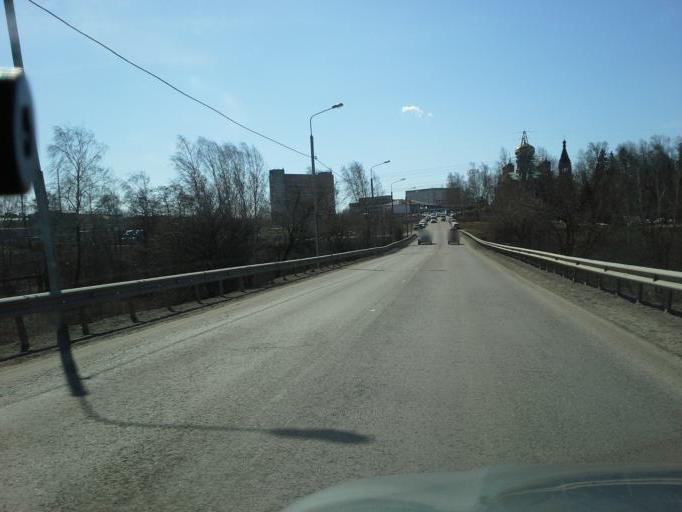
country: RU
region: Moskovskaya
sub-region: Leninskiy Rayon
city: Vnukovo
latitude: 55.6282
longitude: 37.2650
